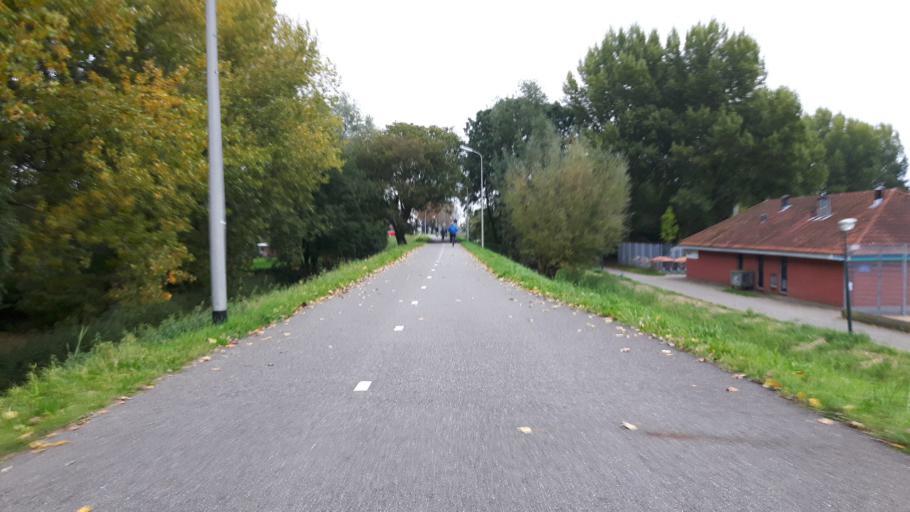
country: NL
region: South Holland
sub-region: Gemeente Vlist
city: Haastrecht
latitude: 52.0041
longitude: 4.7500
